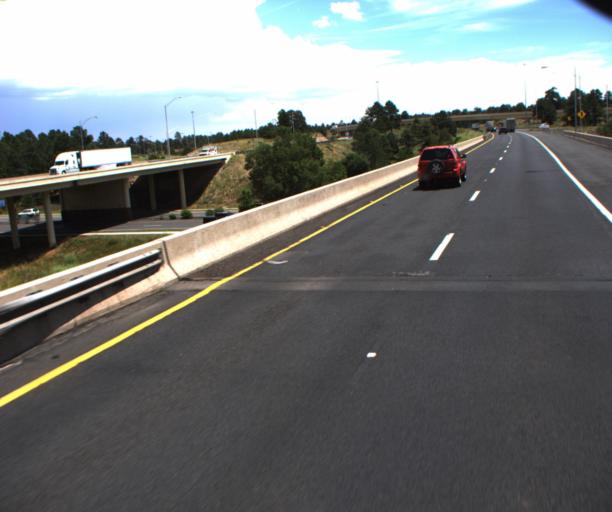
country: US
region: Arizona
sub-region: Coconino County
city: Flagstaff
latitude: 35.1729
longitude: -111.6660
